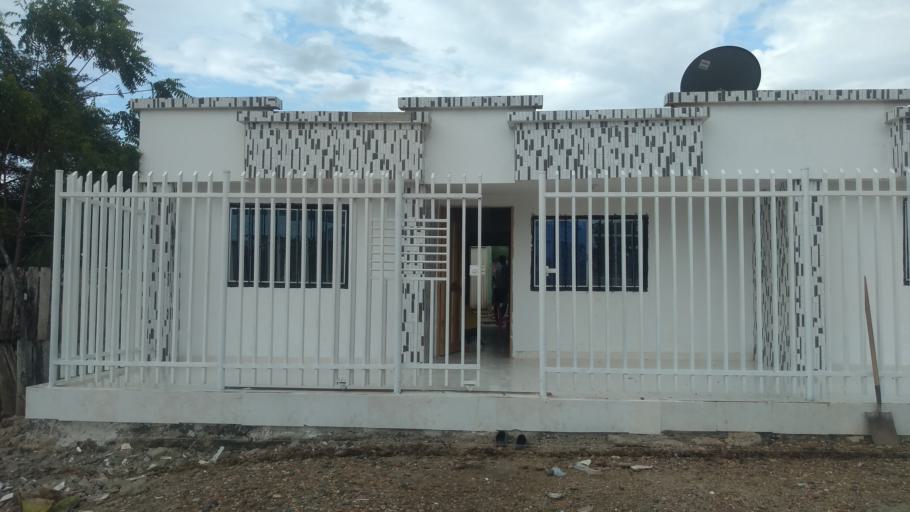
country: CO
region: Magdalena
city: Plato
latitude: 9.7290
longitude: -74.6805
